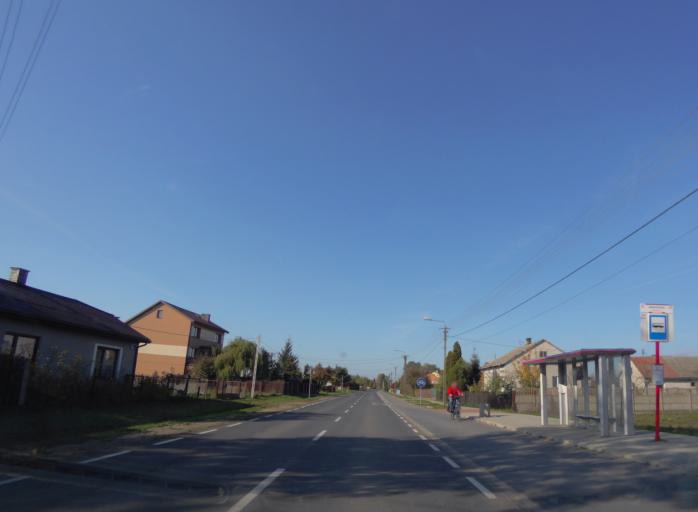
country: PL
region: Masovian Voivodeship
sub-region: Powiat minski
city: Halinow
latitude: 52.1903
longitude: 21.3478
